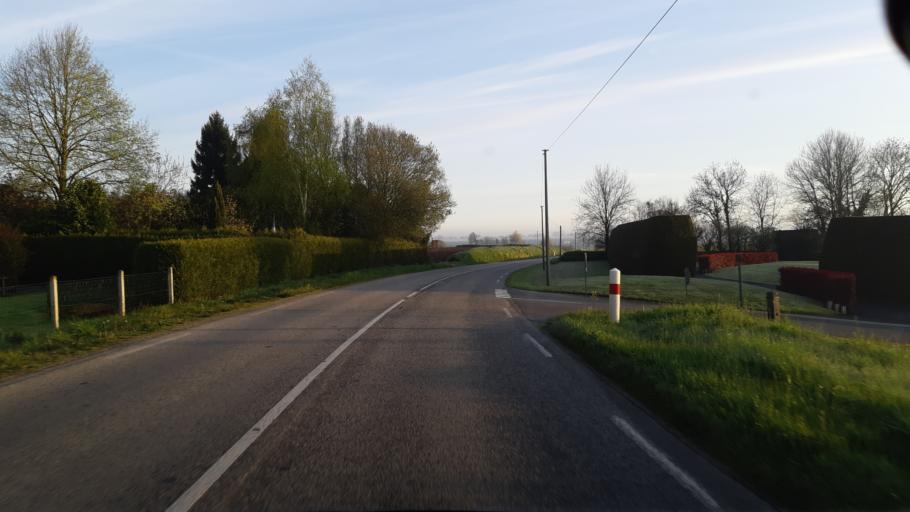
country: FR
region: Lower Normandy
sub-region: Departement de la Manche
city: Agneaux
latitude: 49.0582
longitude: -1.1331
